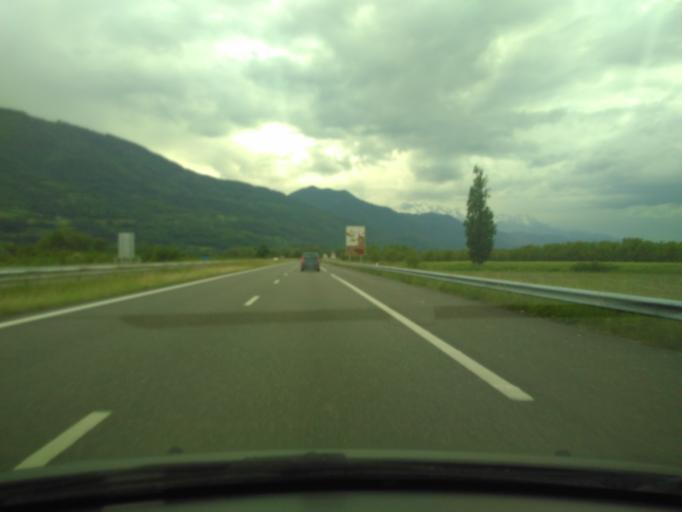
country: FR
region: Rhone-Alpes
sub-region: Departement de l'Isere
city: Pontcharra
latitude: 45.4187
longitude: 5.9983
